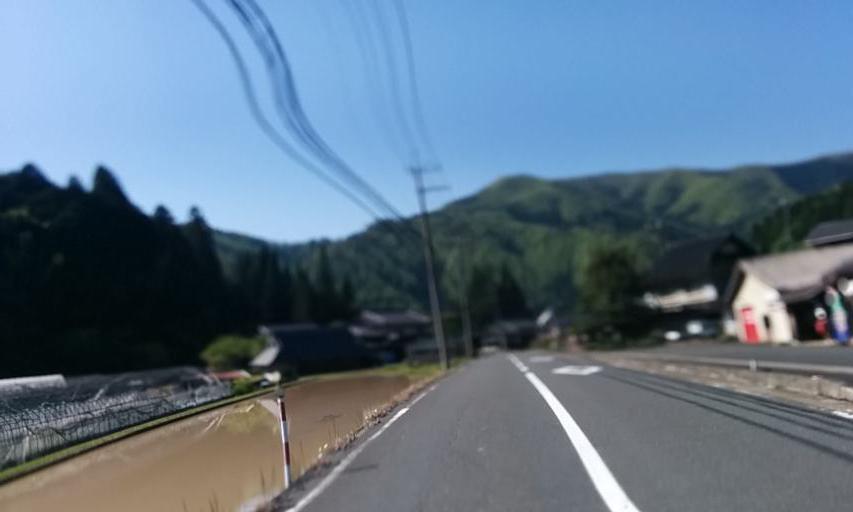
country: JP
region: Kyoto
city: Ayabe
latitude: 35.2611
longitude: 135.4529
